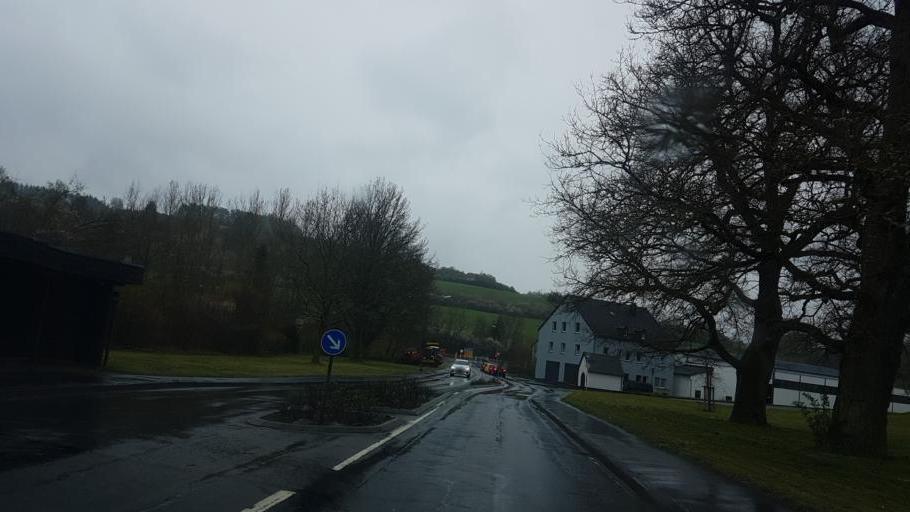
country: DE
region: Rheinland-Pfalz
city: Rockeskyll
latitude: 50.2488
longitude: 6.6966
